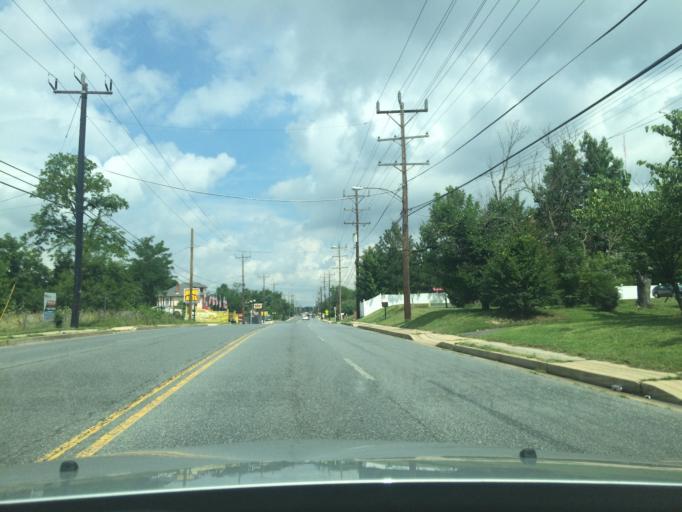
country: US
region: Maryland
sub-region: Prince George's County
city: Coral Hills
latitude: 38.8599
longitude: -76.9096
